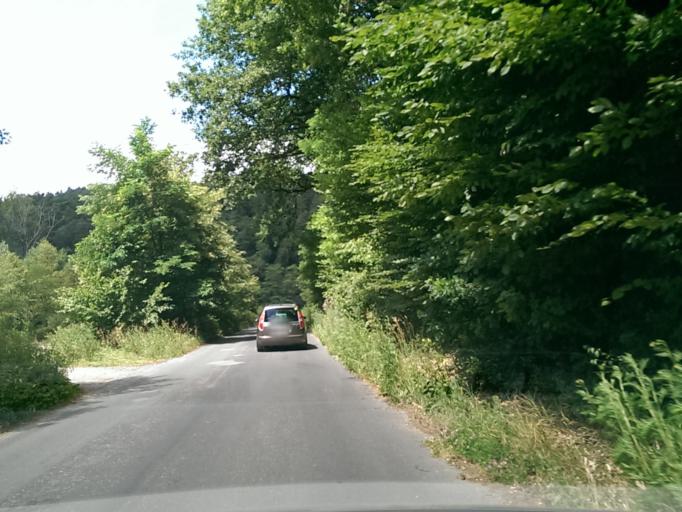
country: CZ
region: Central Bohemia
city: Mseno
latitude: 50.4101
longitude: 14.5713
